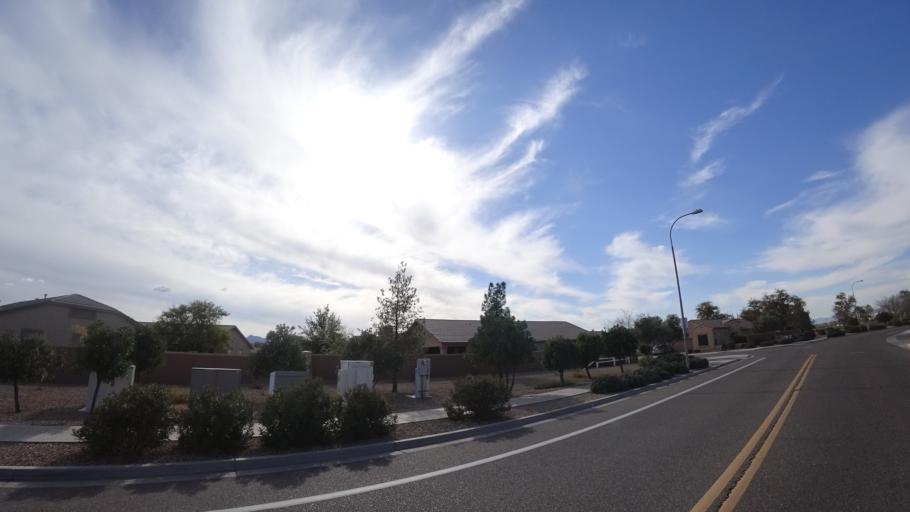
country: US
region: Arizona
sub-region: Maricopa County
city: Tolleson
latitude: 33.4192
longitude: -112.2795
